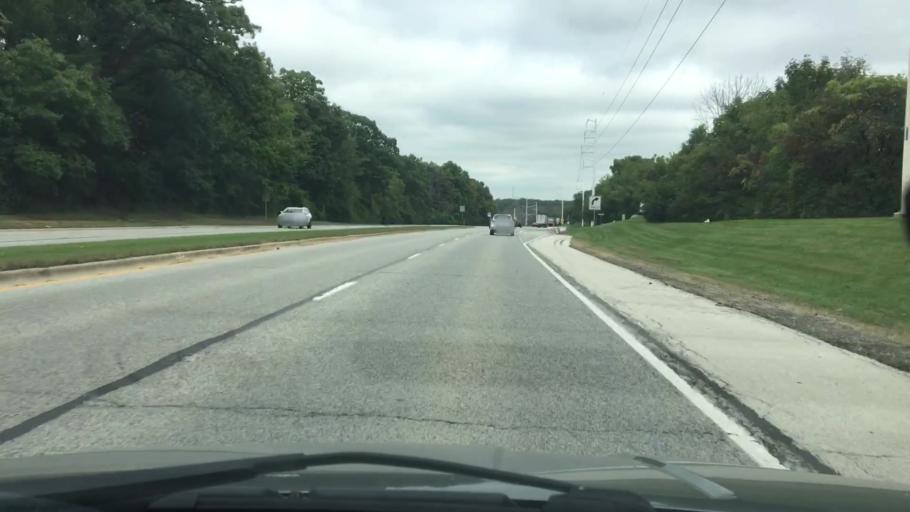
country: US
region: Illinois
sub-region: DuPage County
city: Woodridge
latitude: 41.7494
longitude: -88.0840
